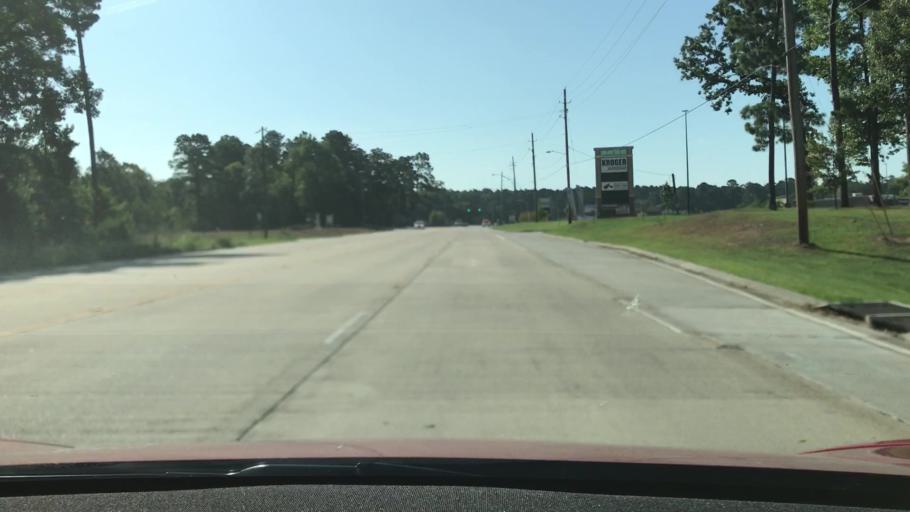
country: US
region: Louisiana
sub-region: Bossier Parish
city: Bossier City
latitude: 32.3977
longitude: -93.7303
